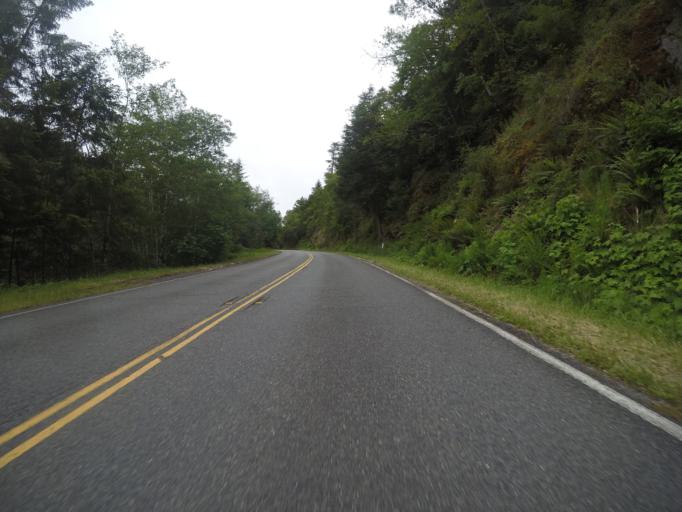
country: US
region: California
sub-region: Del Norte County
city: Bertsch-Oceanview
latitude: 41.7723
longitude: -124.0147
